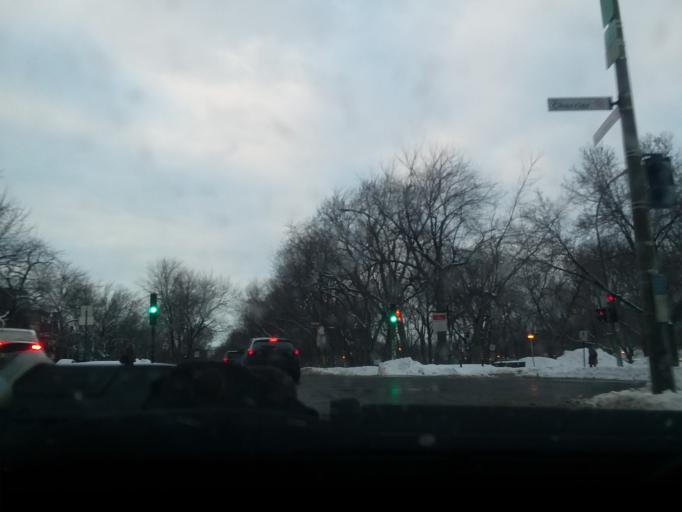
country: CA
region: Quebec
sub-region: Montreal
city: Montreal
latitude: 45.5219
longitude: -73.5664
